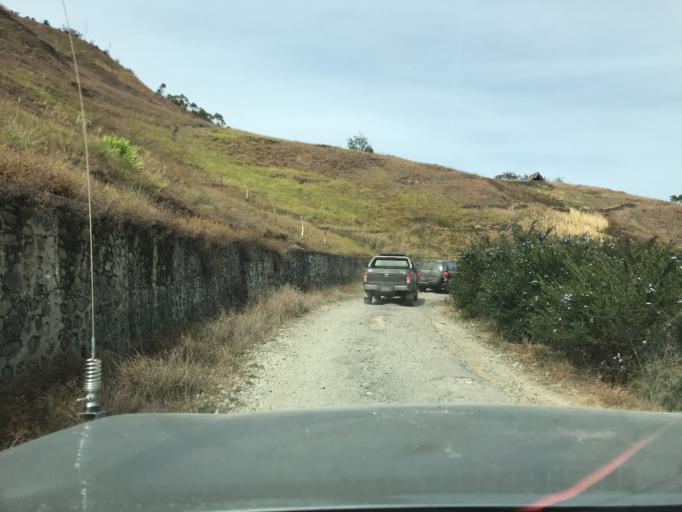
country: TL
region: Ainaro
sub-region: Ainaro
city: Ainaro
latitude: -8.8773
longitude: 125.5883
